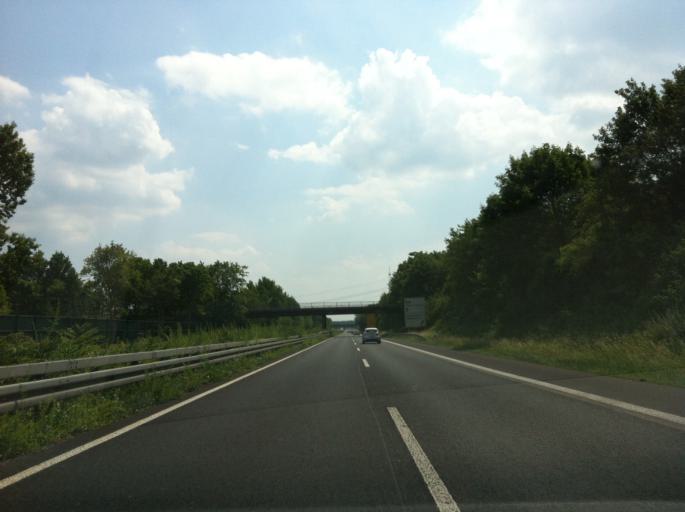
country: DE
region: Hesse
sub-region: Regierungsbezirk Darmstadt
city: Rodgau
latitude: 50.0244
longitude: 8.8932
